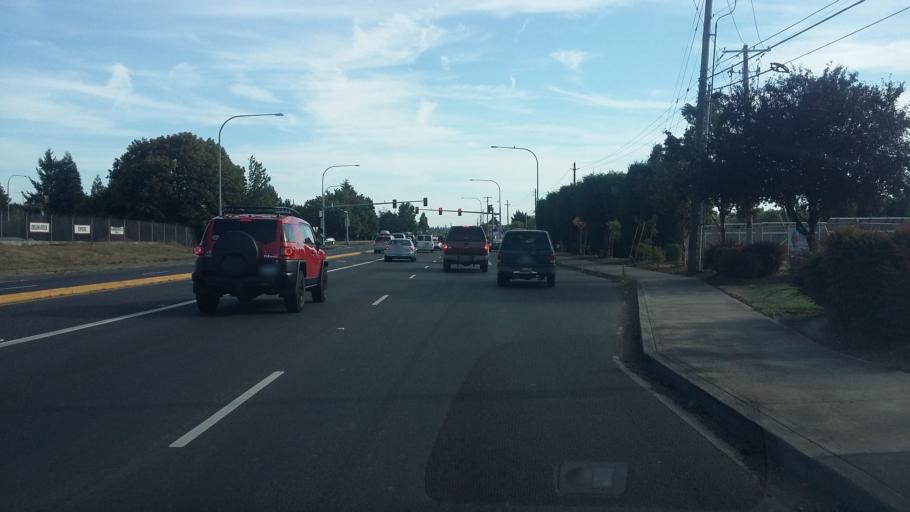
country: US
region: Washington
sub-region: Clark County
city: Orchards
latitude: 45.6834
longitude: -122.5527
